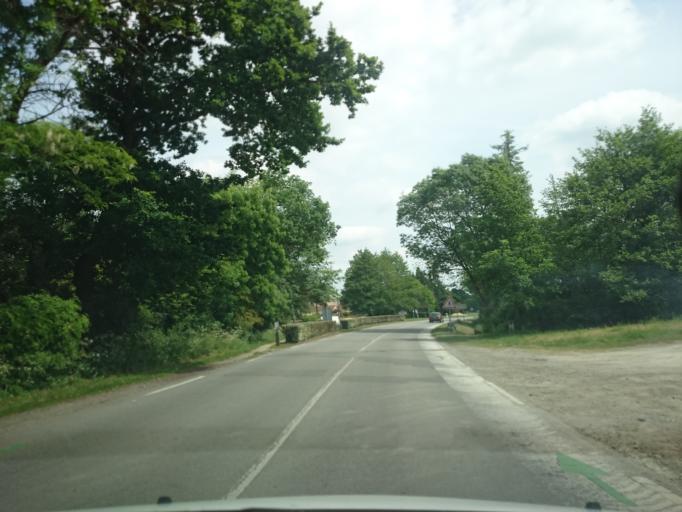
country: FR
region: Pays de la Loire
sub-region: Departement de la Loire-Atlantique
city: La Chevroliere
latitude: 47.1253
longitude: -1.6242
